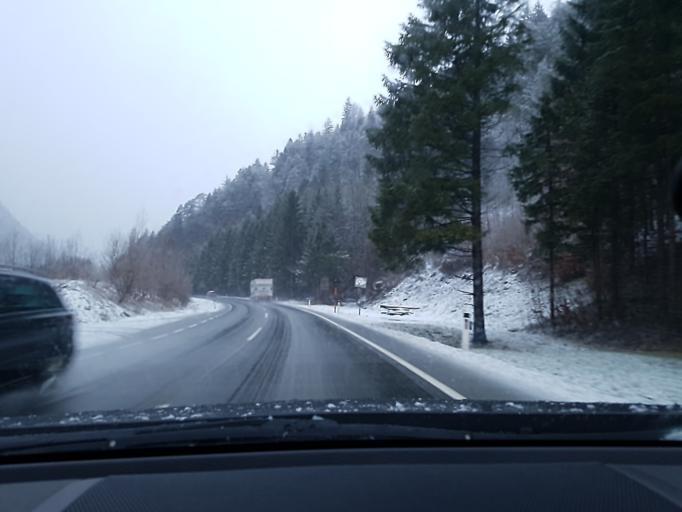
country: AT
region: Salzburg
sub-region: Politischer Bezirk Hallein
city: Scheffau am Tennengebirge
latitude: 47.5860
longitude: 13.2314
